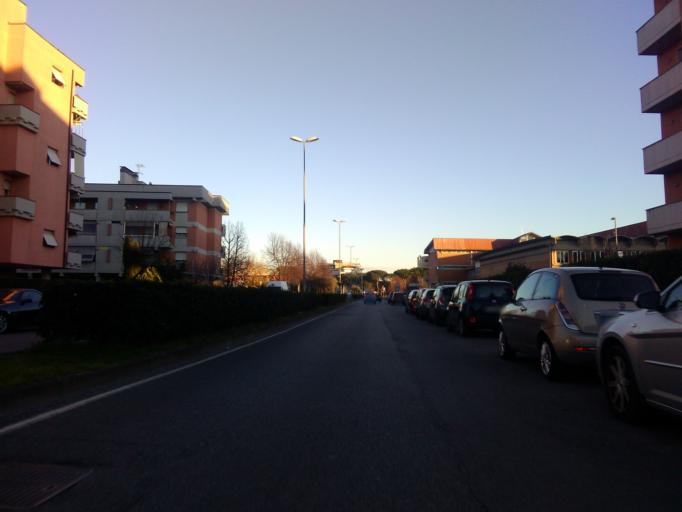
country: IT
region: Tuscany
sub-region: Provincia di Massa-Carrara
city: Carrara
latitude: 44.0544
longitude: 10.0470
